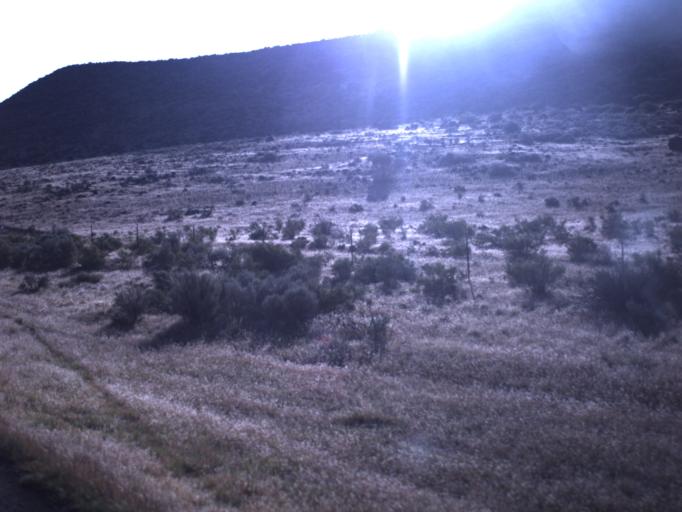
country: US
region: Utah
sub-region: Iron County
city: Enoch
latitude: 37.8499
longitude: -113.0359
